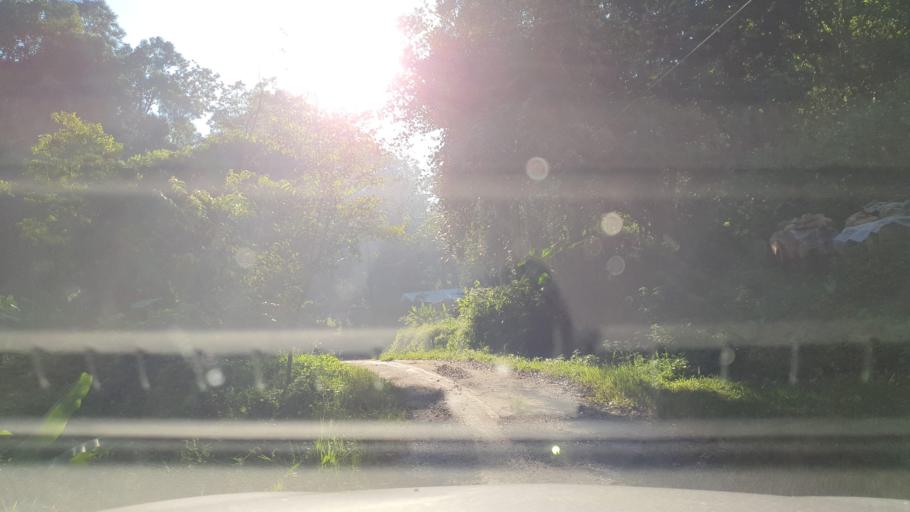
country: TH
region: Chiang Mai
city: Mae On
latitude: 18.8159
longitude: 99.3386
